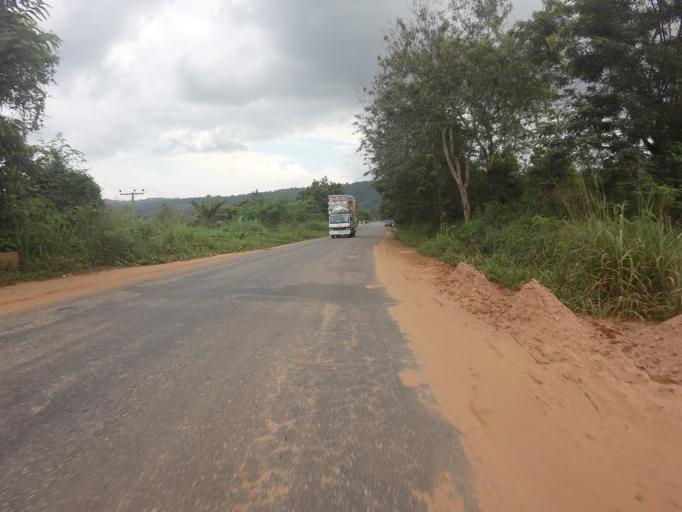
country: GH
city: Akropong
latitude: 5.9602
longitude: -0.1331
